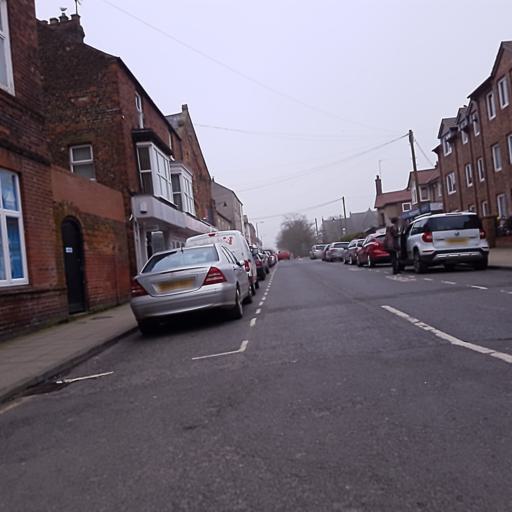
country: GB
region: England
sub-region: North Yorkshire
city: Filey
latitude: 54.2097
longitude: -0.2890
